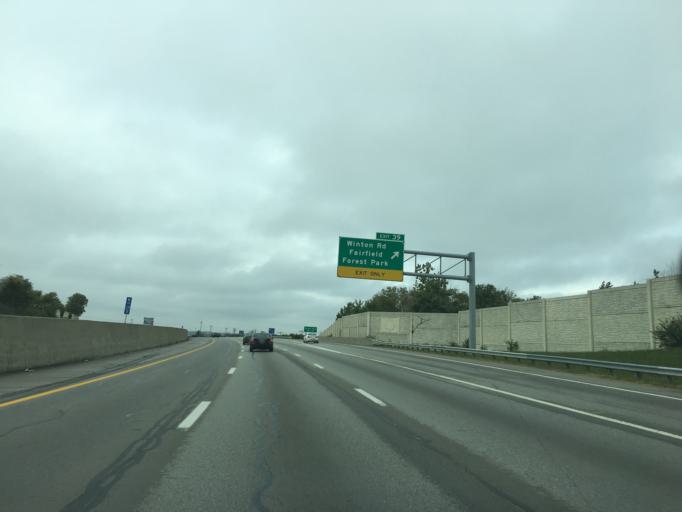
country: US
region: Ohio
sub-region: Hamilton County
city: Forest Park
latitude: 39.3002
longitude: -84.5109
